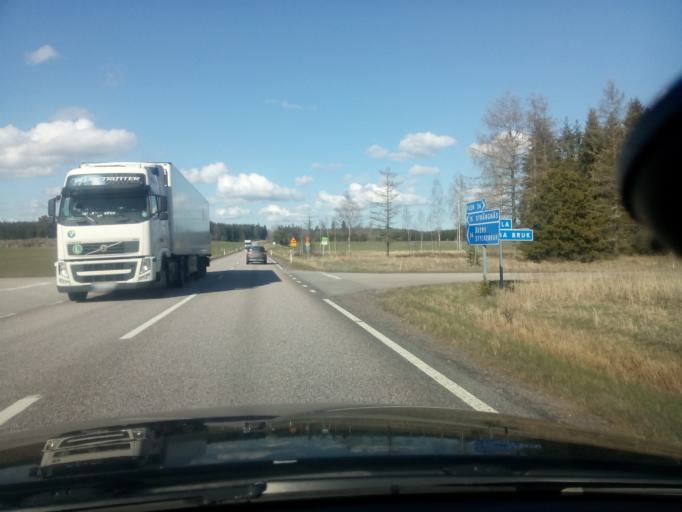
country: SE
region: Soedermanland
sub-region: Strangnas Kommun
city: Akers Styckebruk
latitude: 59.2585
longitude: 16.9424
